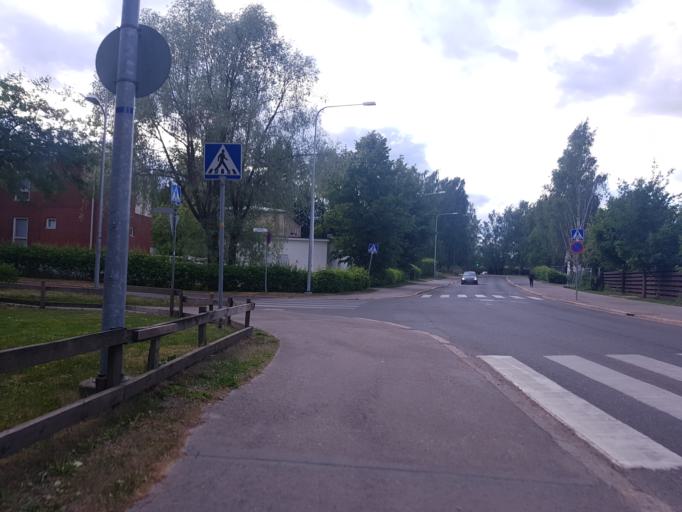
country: FI
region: Uusimaa
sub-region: Helsinki
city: Vantaa
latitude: 60.2478
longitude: 24.9910
